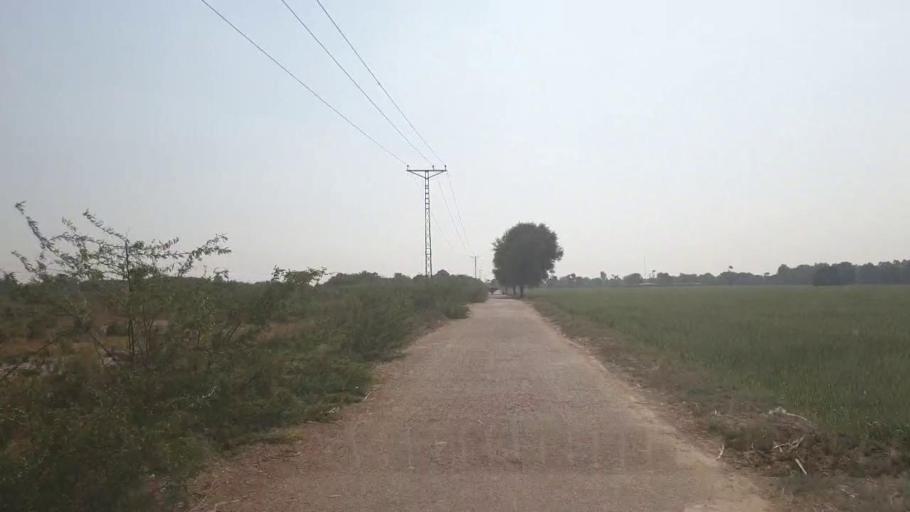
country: PK
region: Sindh
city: Mirpur Khas
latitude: 25.4950
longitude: 68.8821
